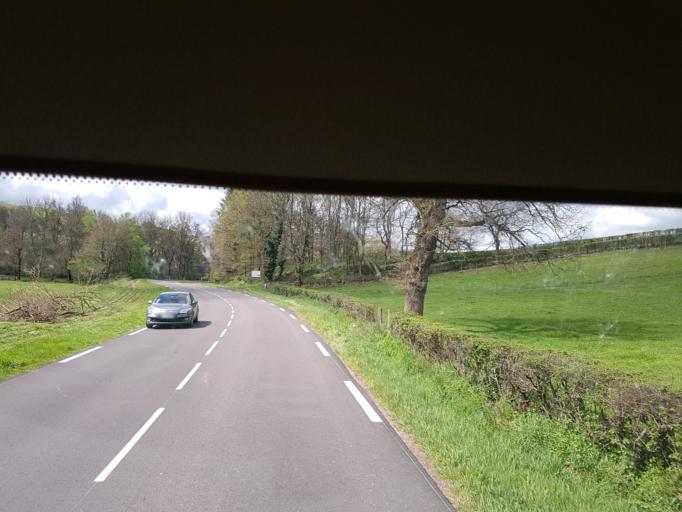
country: FR
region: Bourgogne
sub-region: Departement de Saone-et-Loire
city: La Clayette
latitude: 46.2860
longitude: 4.3444
